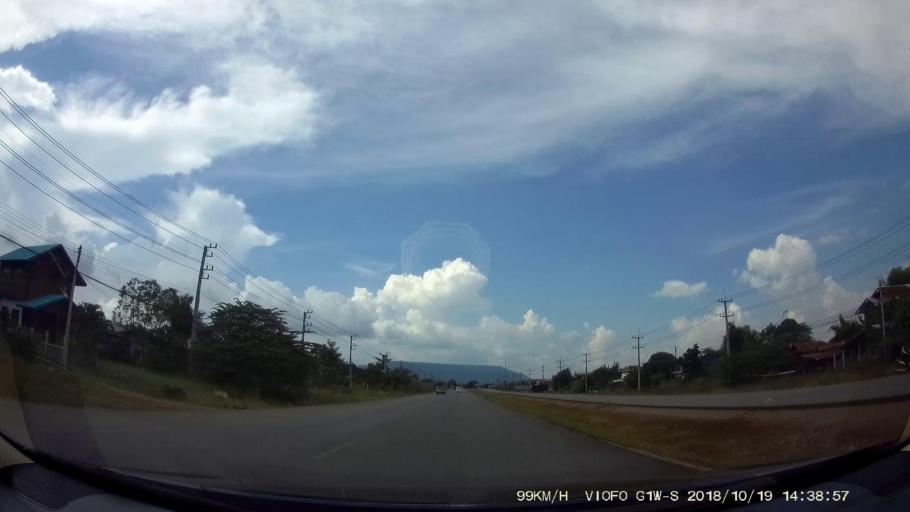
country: TH
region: Chaiyaphum
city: Kaeng Khro
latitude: 16.2200
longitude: 102.1978
